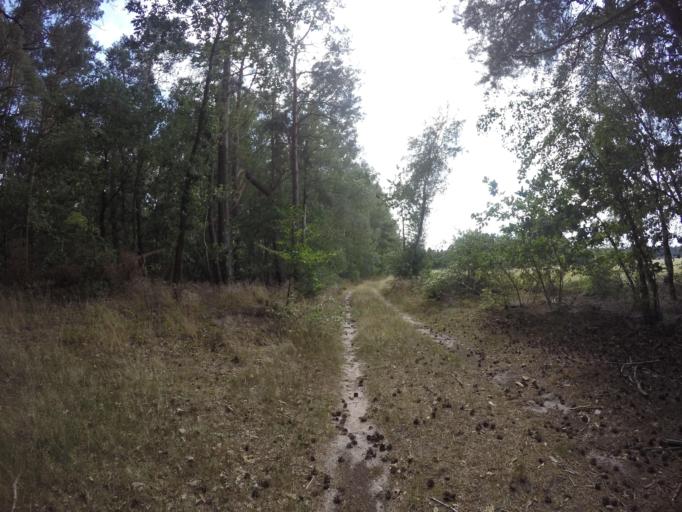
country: DE
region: Lower Saxony
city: Bleckede
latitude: 53.2535
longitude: 10.7230
